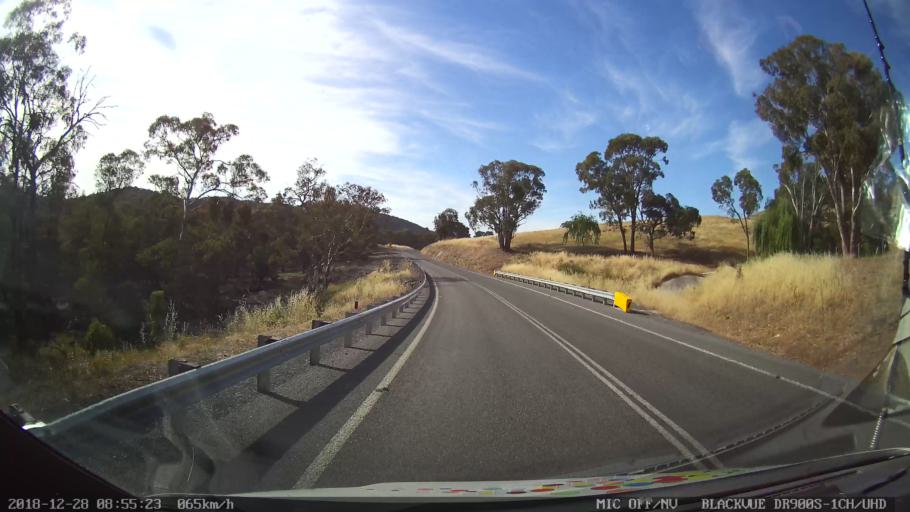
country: AU
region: New South Wales
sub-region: Upper Lachlan Shire
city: Crookwell
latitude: -34.1004
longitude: 149.3324
